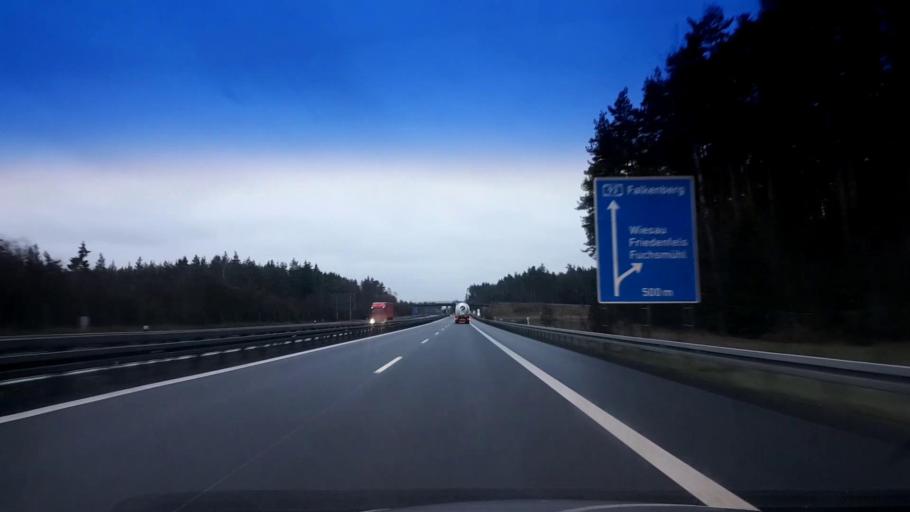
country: DE
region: Bavaria
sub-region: Upper Palatinate
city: Wiesau
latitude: 49.9194
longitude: 12.2223
